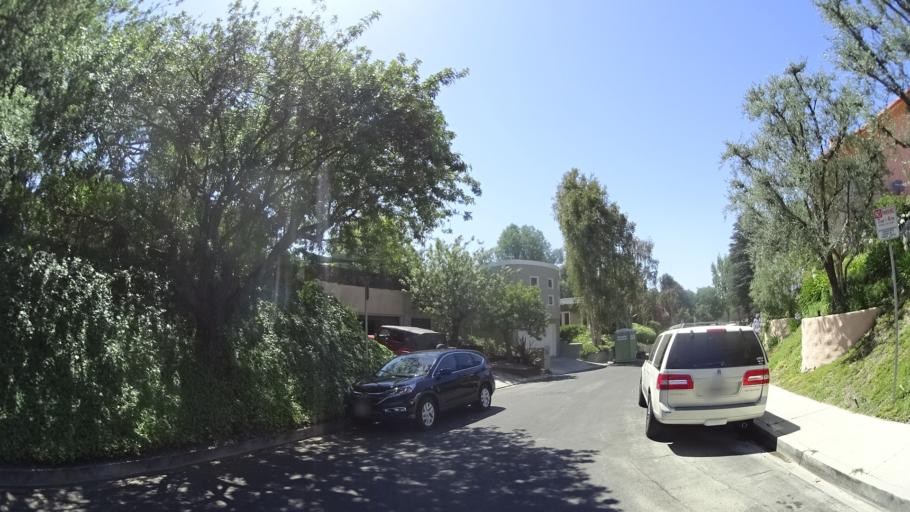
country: US
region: California
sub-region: Los Angeles County
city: Sherman Oaks
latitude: 34.1472
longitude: -118.4918
